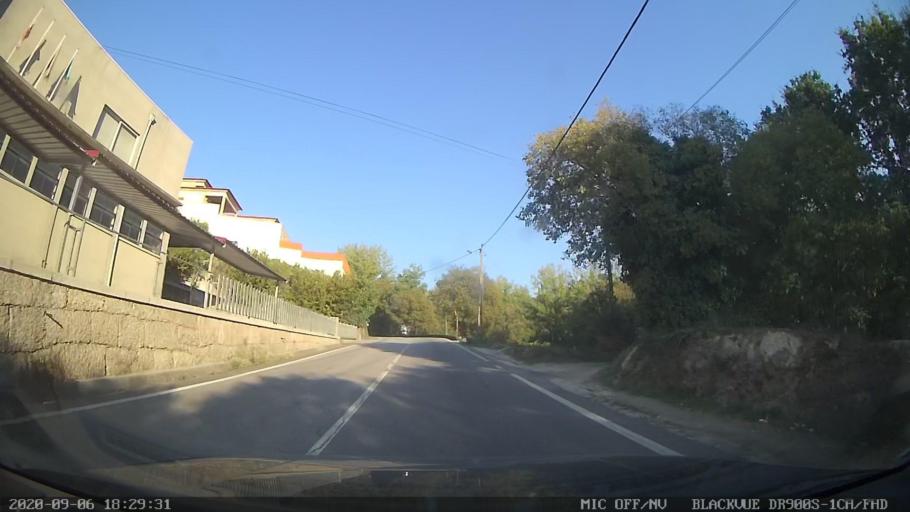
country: PT
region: Porto
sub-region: Amarante
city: Amarante
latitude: 41.2641
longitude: -8.0657
